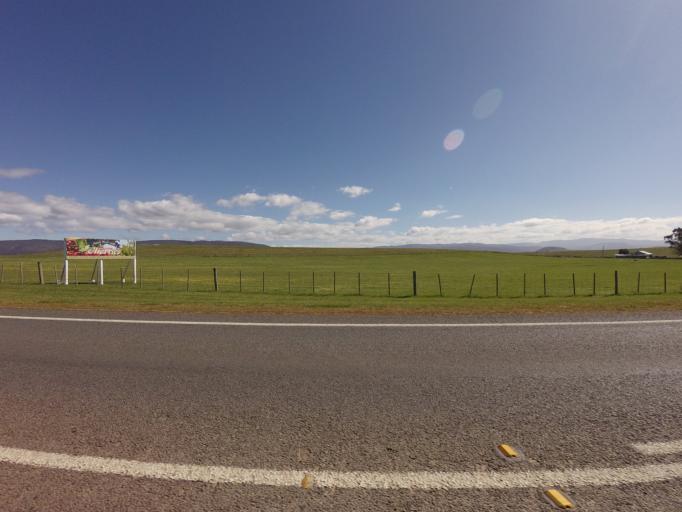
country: AU
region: Tasmania
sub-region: Derwent Valley
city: New Norfolk
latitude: -42.7033
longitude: 146.9425
